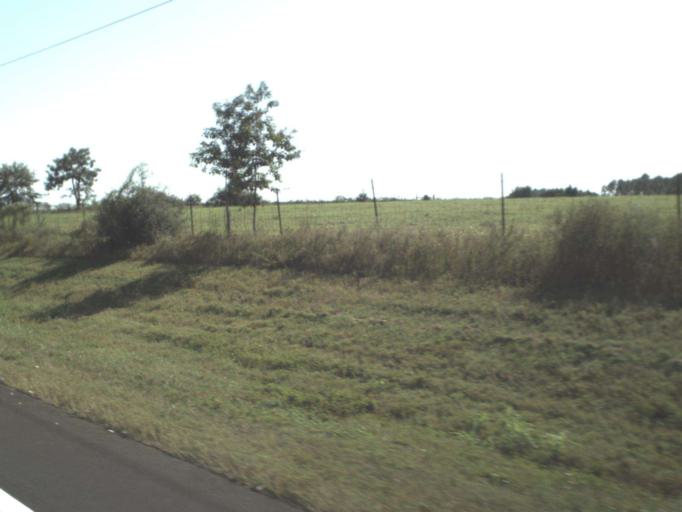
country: US
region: Florida
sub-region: Walton County
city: DeFuniak Springs
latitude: 30.8327
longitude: -86.2326
